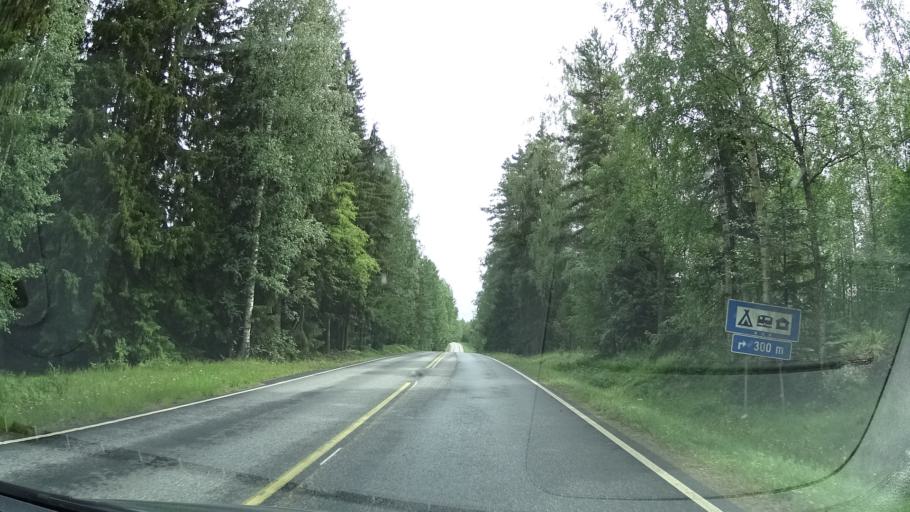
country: FI
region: Pirkanmaa
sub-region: Etelae-Pirkanmaa
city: Urjala
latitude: 61.0868
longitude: 23.3987
